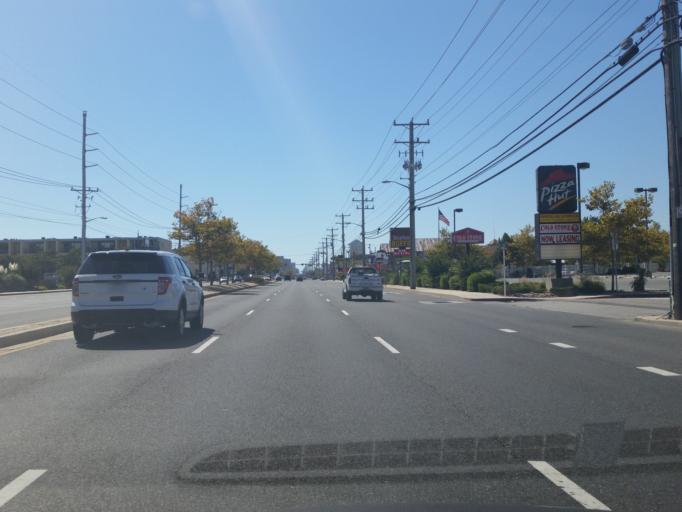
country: US
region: Delaware
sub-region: Sussex County
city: Bethany Beach
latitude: 38.4378
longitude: -75.0541
